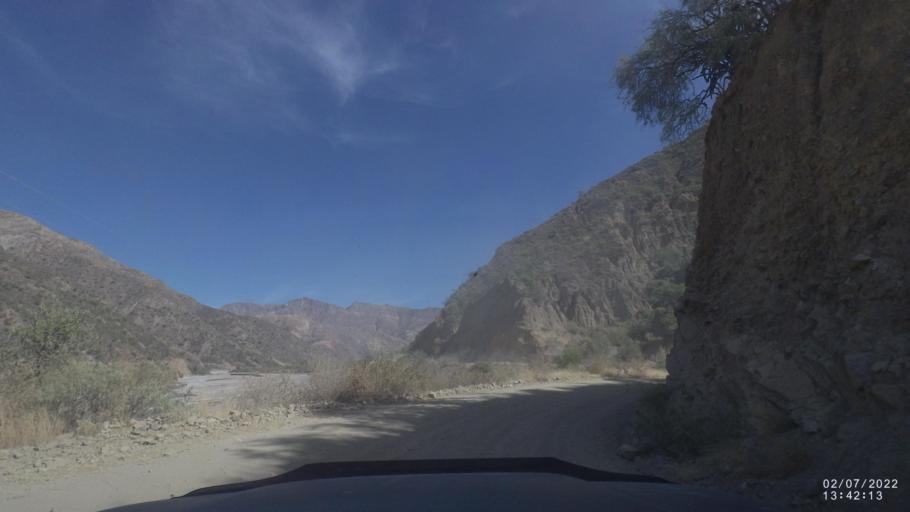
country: BO
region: Cochabamba
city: Irpa Irpa
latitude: -17.8000
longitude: -66.3550
